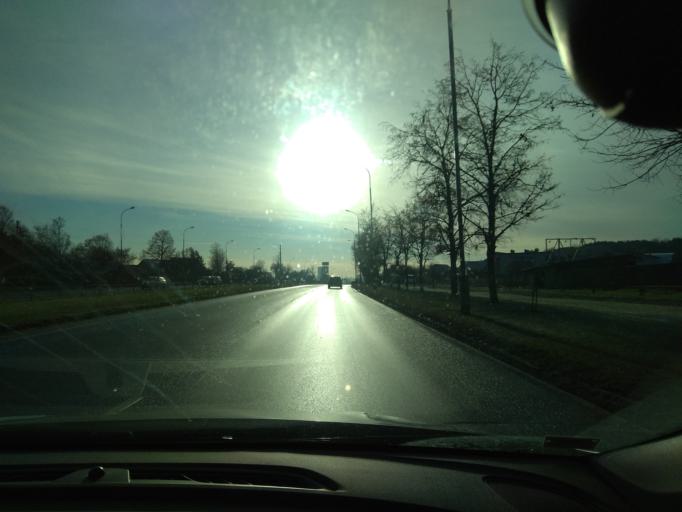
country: LT
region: Vilnius County
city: Seskine
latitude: 54.7191
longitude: 25.2707
